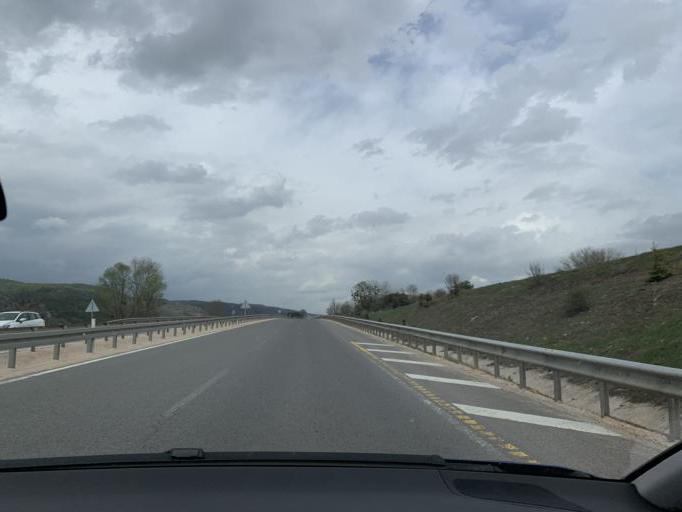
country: TR
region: Bolu
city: Gerede
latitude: 40.7893
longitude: 32.1299
